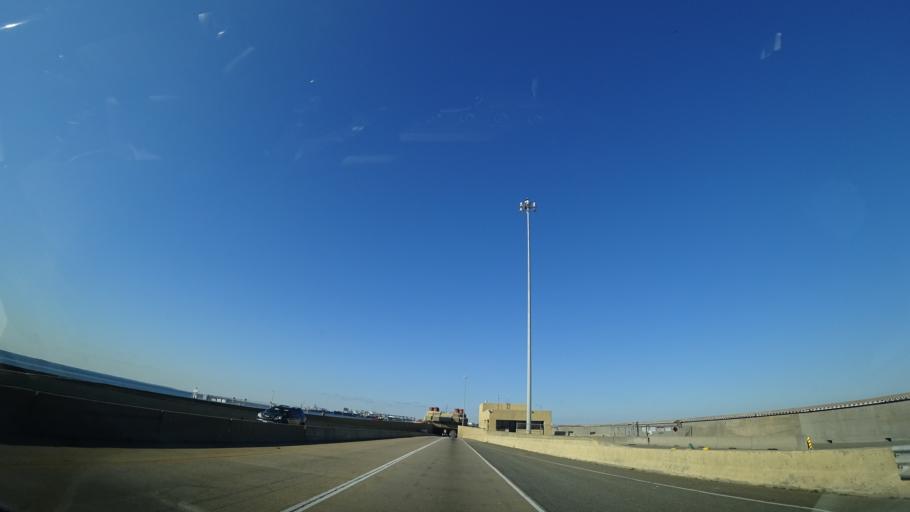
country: US
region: Virginia
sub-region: City of Newport News
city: Newport News
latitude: 36.9444
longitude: -76.4034
